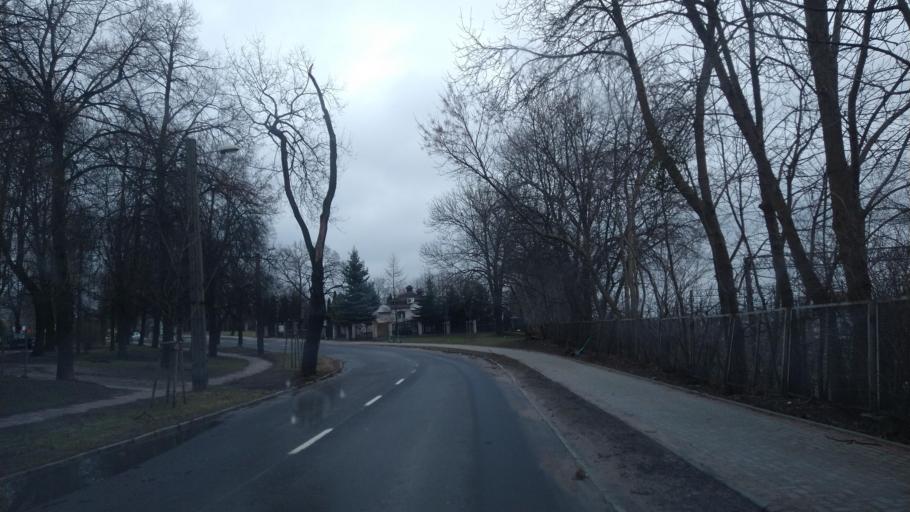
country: PL
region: Warmian-Masurian Voivodeship
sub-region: Powiat olsztynski
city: Olsztyn
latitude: 53.7861
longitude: 20.4956
